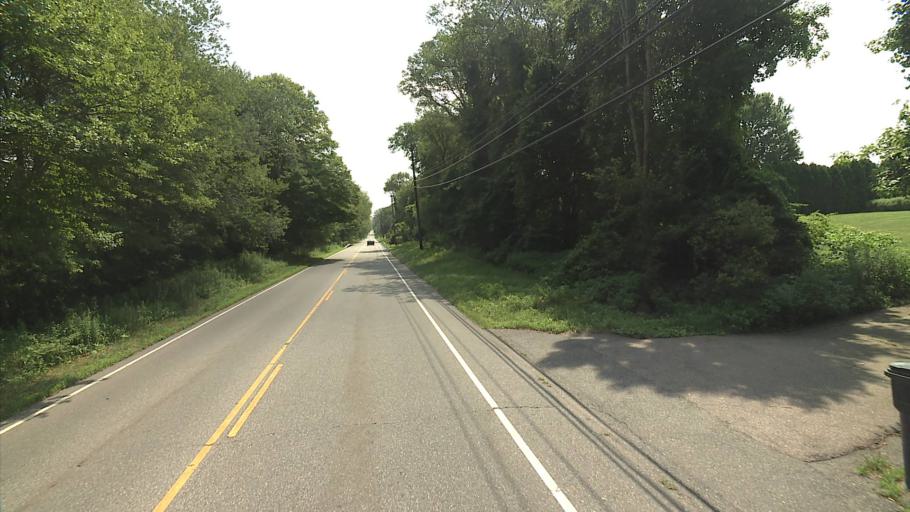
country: US
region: Connecticut
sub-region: New London County
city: Preston City
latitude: 41.5311
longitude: -71.9672
